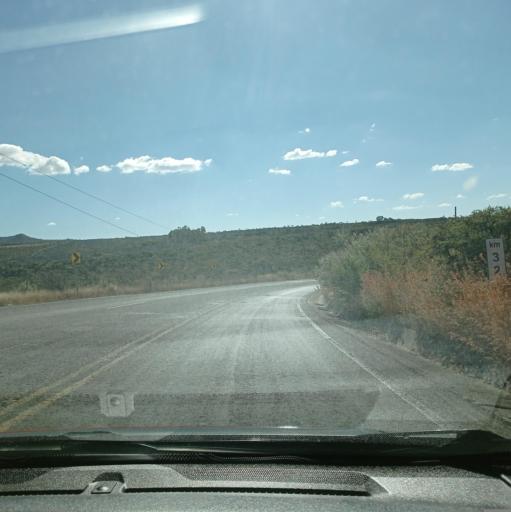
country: MX
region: Jalisco
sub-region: San Julian
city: Colonia Veintitres de Mayo
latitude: 21.0046
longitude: -102.2719
